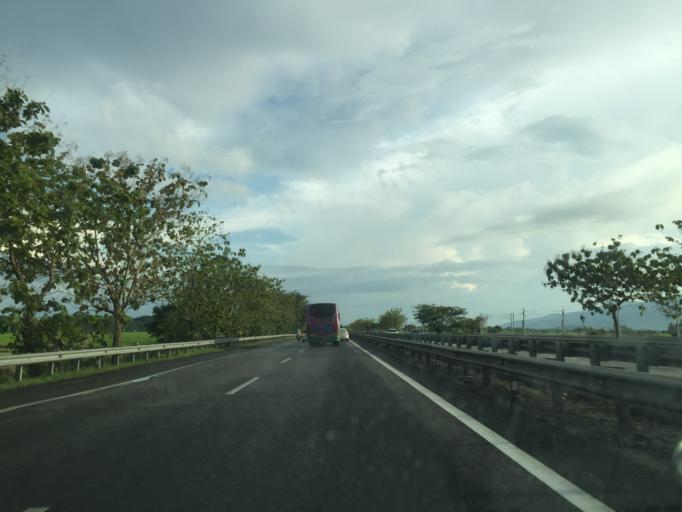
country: MY
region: Kedah
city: Gurun
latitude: 5.9226
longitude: 100.4657
